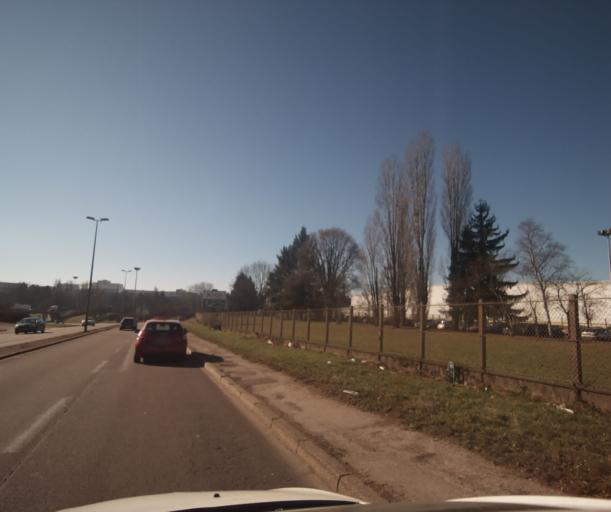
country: FR
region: Franche-Comte
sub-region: Departement du Doubs
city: Avanne-Aveney
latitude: 47.2292
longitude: 5.9808
